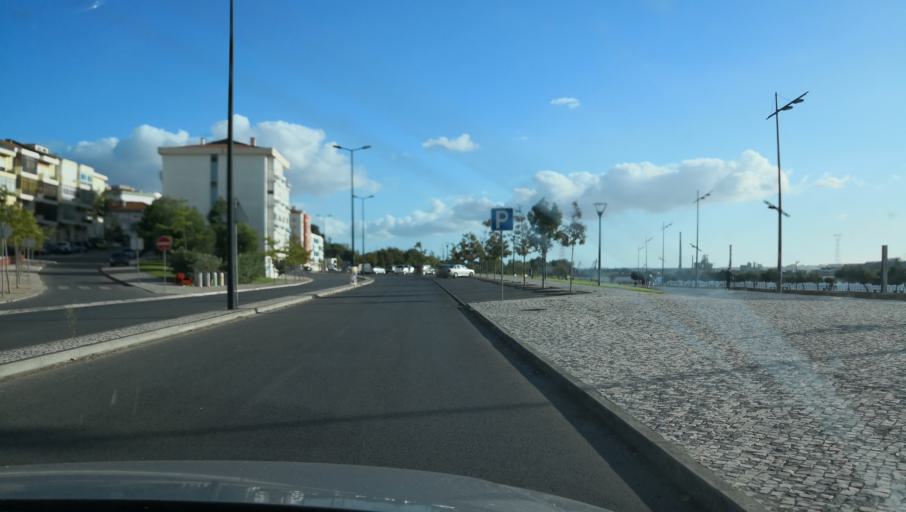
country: PT
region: Setubal
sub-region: Barreiro
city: Barreiro
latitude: 38.6479
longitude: -9.0649
